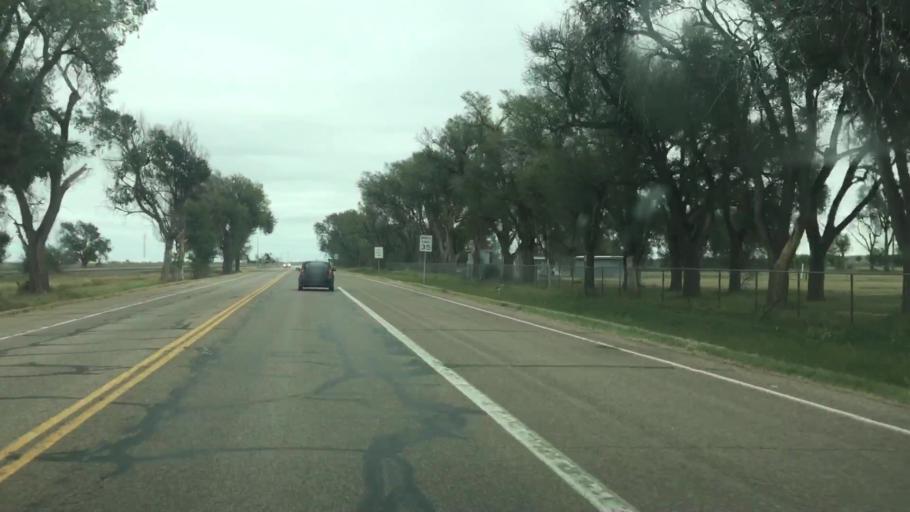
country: US
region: Colorado
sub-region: Prowers County
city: Lamar
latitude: 38.0622
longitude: -102.3055
